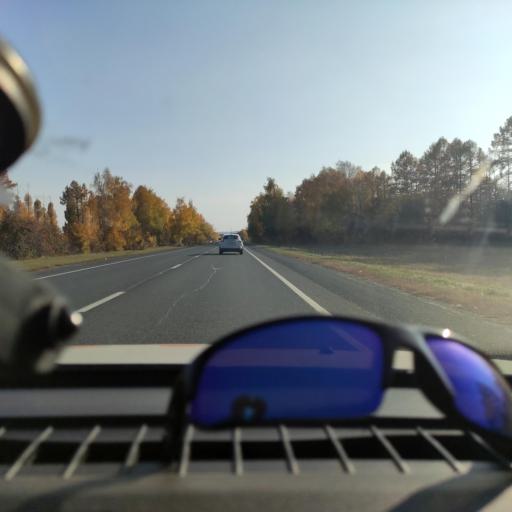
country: RU
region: Samara
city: Volzhskiy
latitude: 53.4625
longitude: 50.1275
